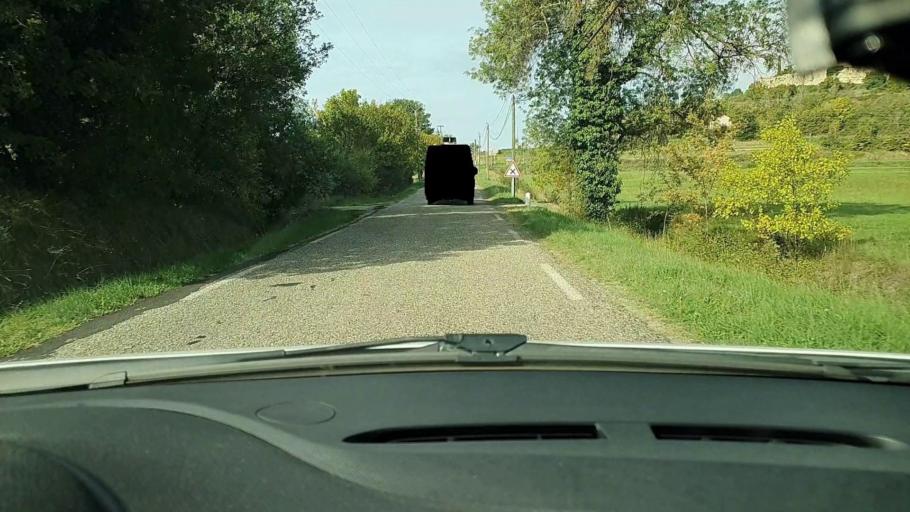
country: FR
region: Languedoc-Roussillon
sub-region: Departement du Gard
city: Goudargues
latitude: 44.1499
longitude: 4.3707
